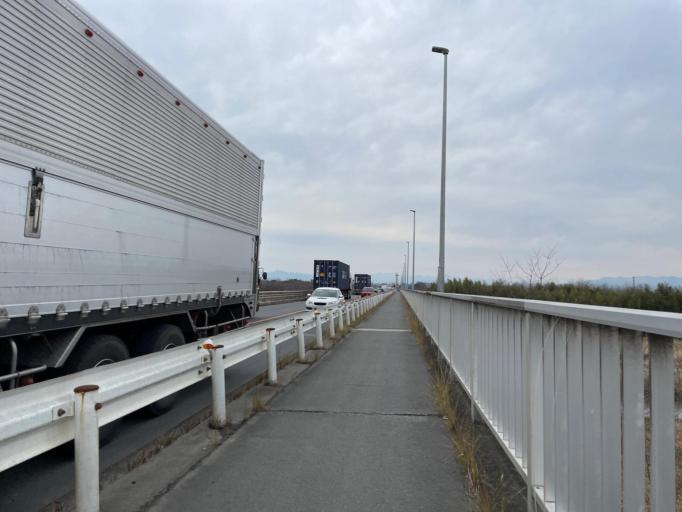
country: JP
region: Gunma
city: Fujioka
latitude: 36.2367
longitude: 139.0975
